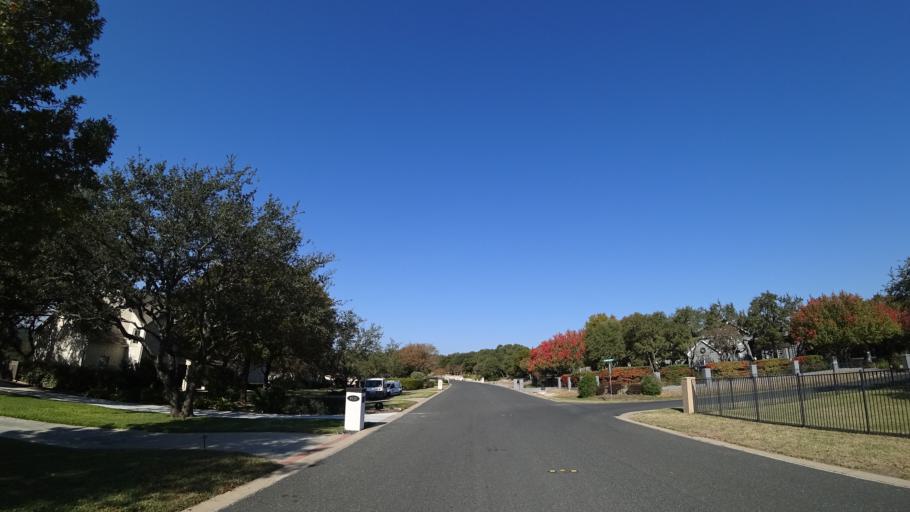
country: US
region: Texas
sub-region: Williamson County
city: Anderson Mill
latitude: 30.3789
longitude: -97.8273
